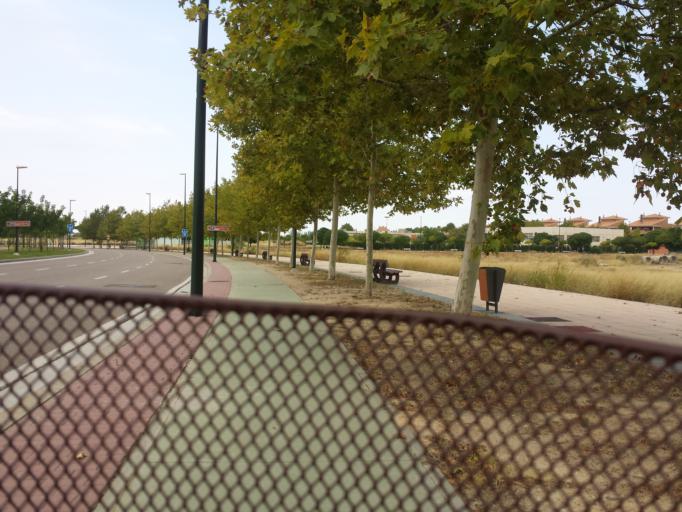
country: ES
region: Aragon
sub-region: Provincia de Zaragoza
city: Montecanal
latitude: 41.6237
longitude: -0.9392
